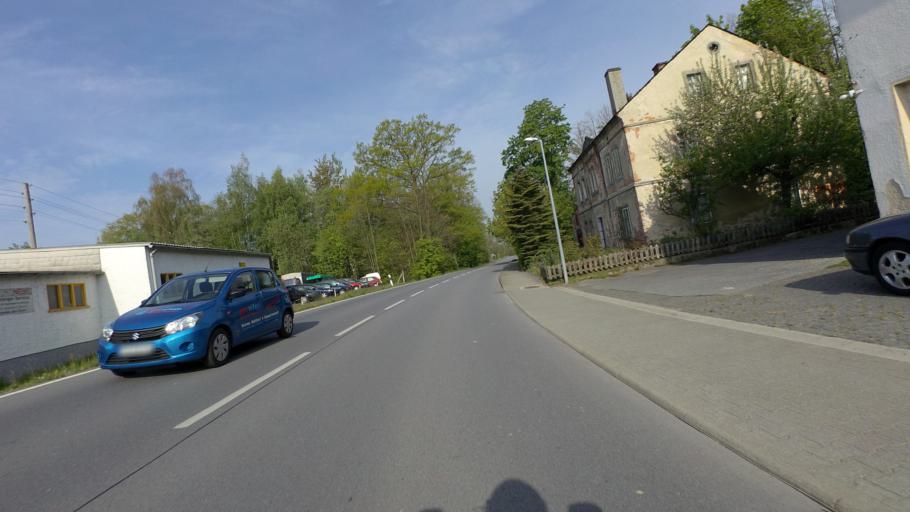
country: DE
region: Saxony
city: Stolpen
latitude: 51.0396
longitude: 14.1306
